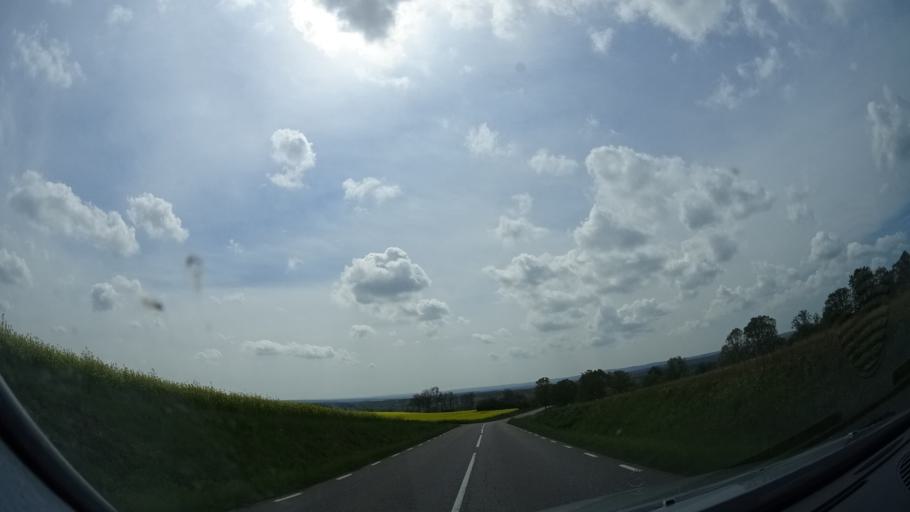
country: SE
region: Skane
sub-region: Hoors Kommun
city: Loberod
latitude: 55.7346
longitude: 13.4953
